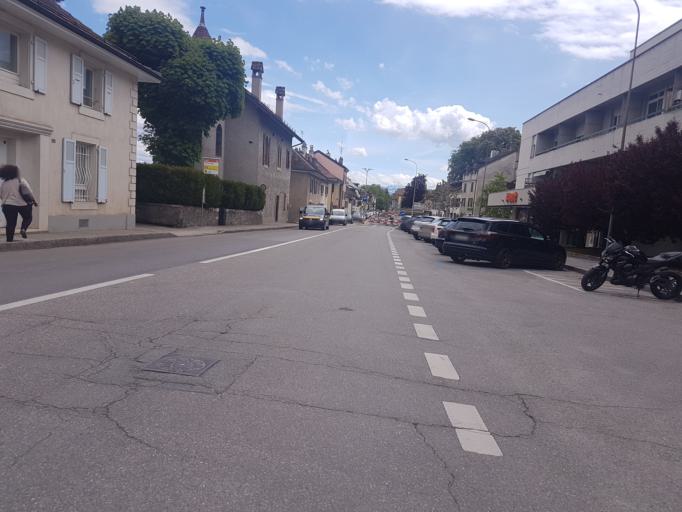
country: CH
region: Geneva
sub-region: Geneva
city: Versoix
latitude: 46.2801
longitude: 6.1673
